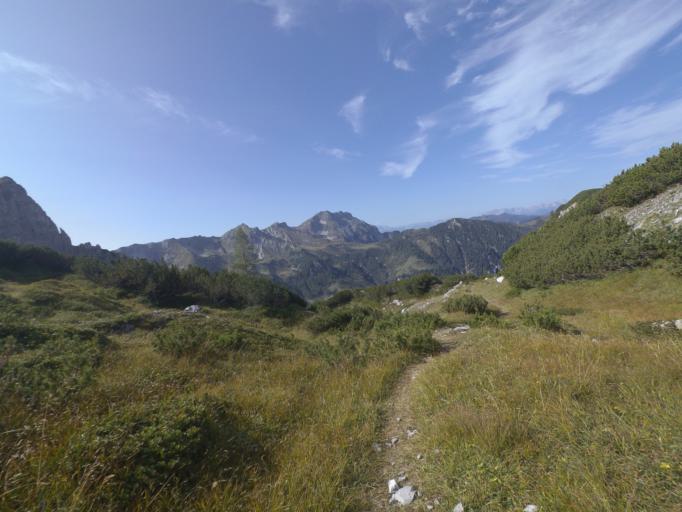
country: AT
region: Salzburg
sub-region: Politischer Bezirk Sankt Johann im Pongau
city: Kleinarl
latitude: 47.2309
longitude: 13.4049
